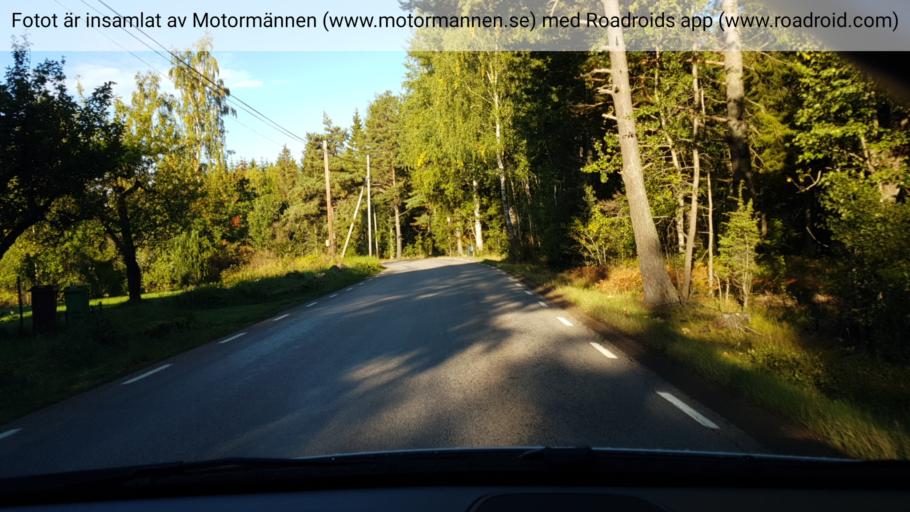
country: SE
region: Vaestra Goetaland
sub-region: Skovde Kommun
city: Stopen
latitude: 58.5376
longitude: 13.7251
